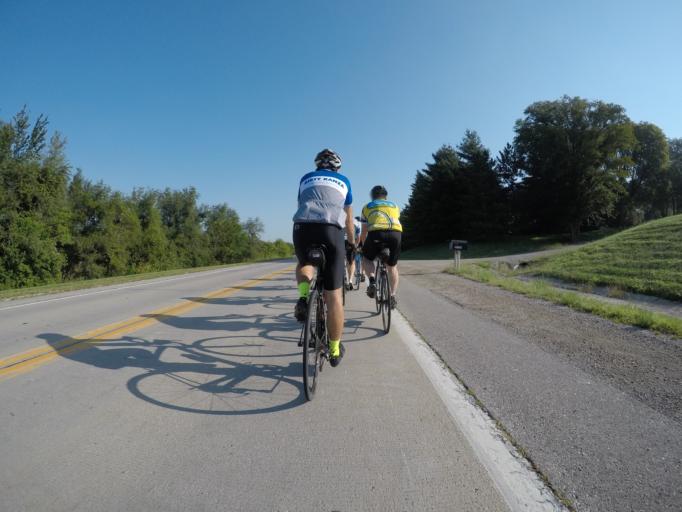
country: US
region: Missouri
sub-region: Platte County
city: Weston
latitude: 39.3769
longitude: -94.8640
